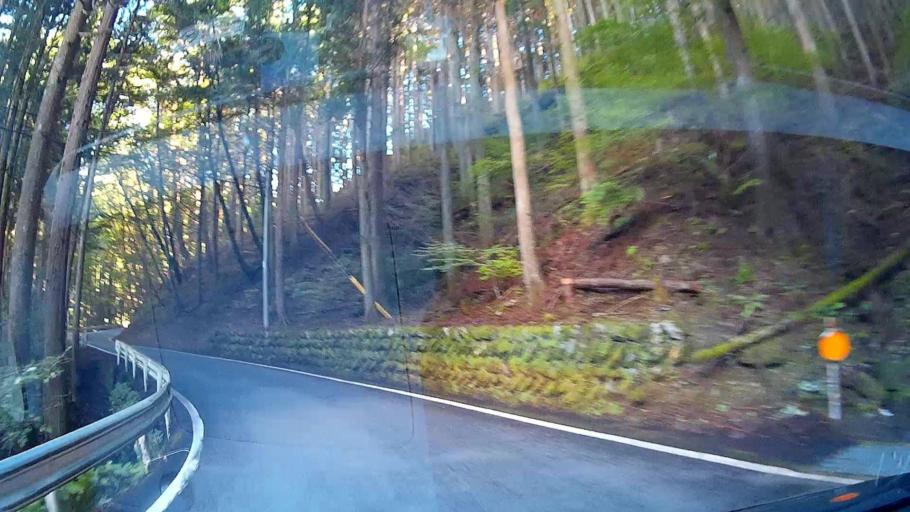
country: JP
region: Shizuoka
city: Shizuoka-shi
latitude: 35.2059
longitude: 138.2296
